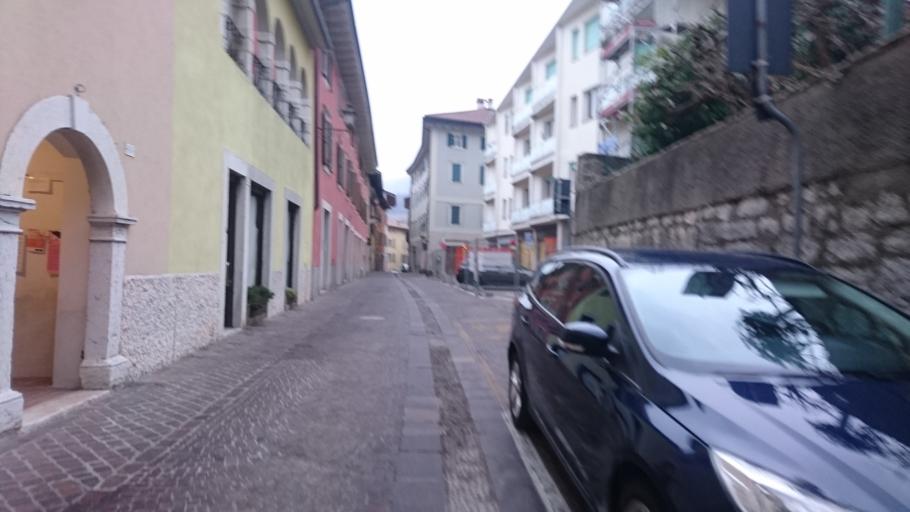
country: IT
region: Trentino-Alto Adige
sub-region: Provincia di Trento
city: Mori
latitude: 45.8534
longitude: 10.9790
